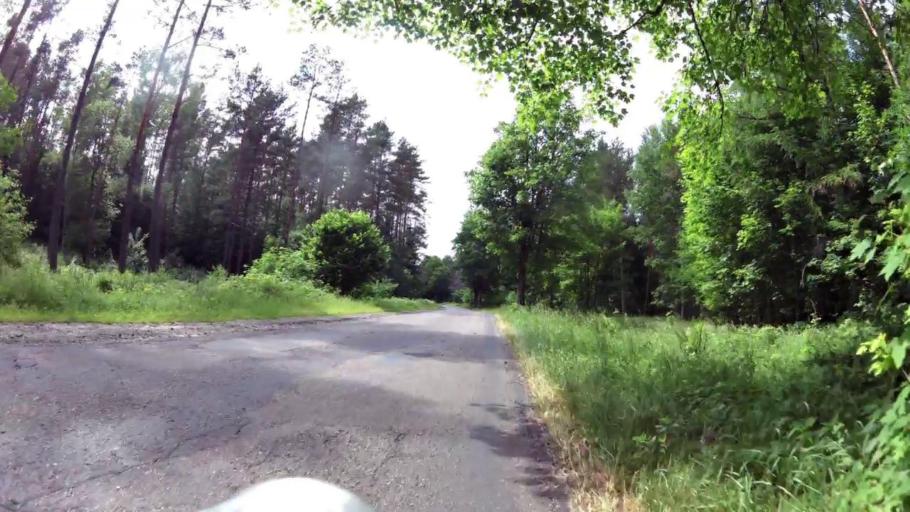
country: PL
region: West Pomeranian Voivodeship
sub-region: Powiat szczecinecki
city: Bialy Bor
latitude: 53.9562
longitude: 16.7496
